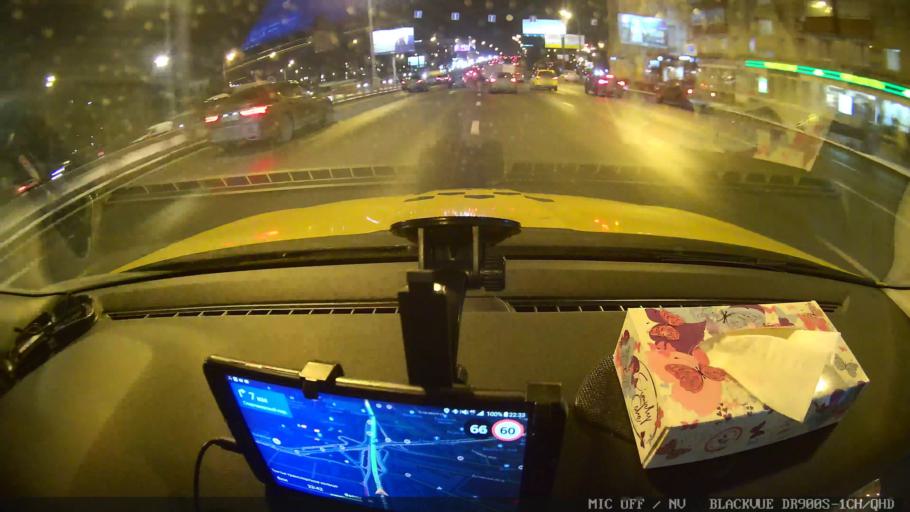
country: RU
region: Moscow
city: Mar'ina Roshcha
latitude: 55.7908
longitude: 37.5820
